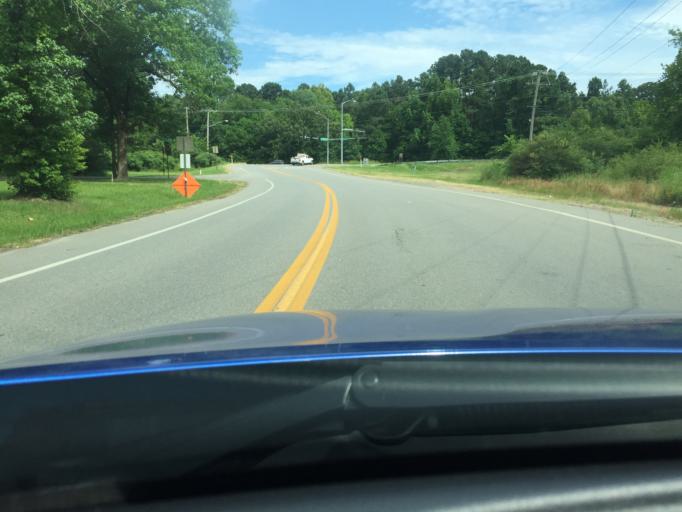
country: US
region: Arkansas
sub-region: Pulaski County
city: Maumelle
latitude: 34.8032
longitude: -92.4339
